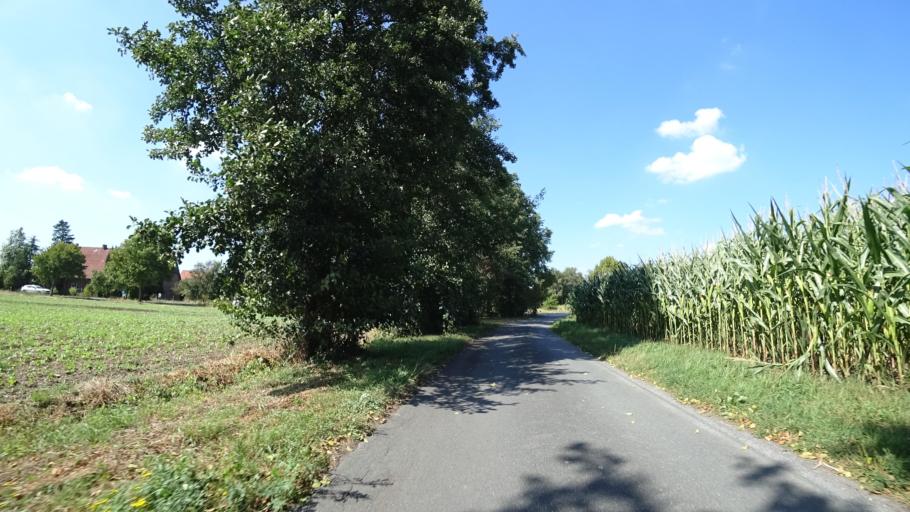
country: DE
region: North Rhine-Westphalia
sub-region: Regierungsbezirk Detmold
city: Rheda-Wiedenbruck
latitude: 51.8879
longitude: 8.2823
